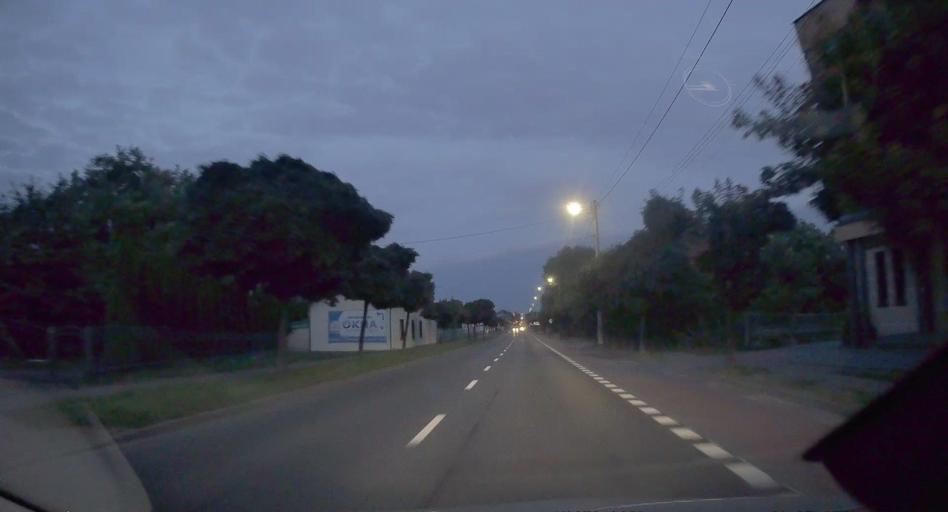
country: PL
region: Silesian Voivodeship
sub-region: Powiat klobucki
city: Klobuck
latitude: 50.9040
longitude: 18.9272
